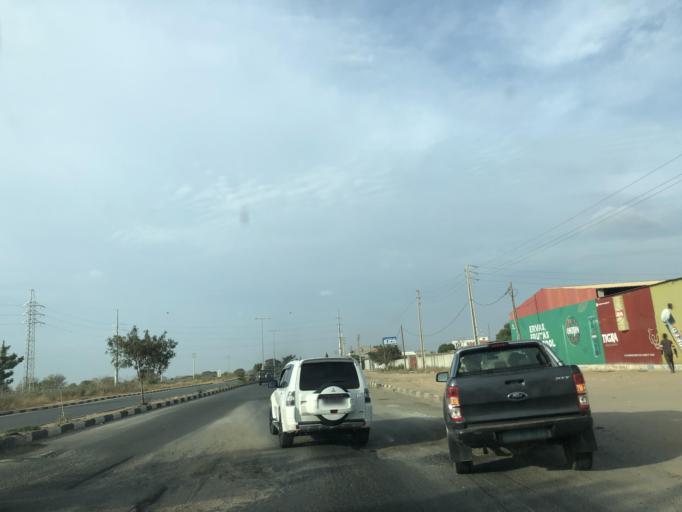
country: AO
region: Luanda
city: Luanda
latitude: -8.9415
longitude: 13.2945
